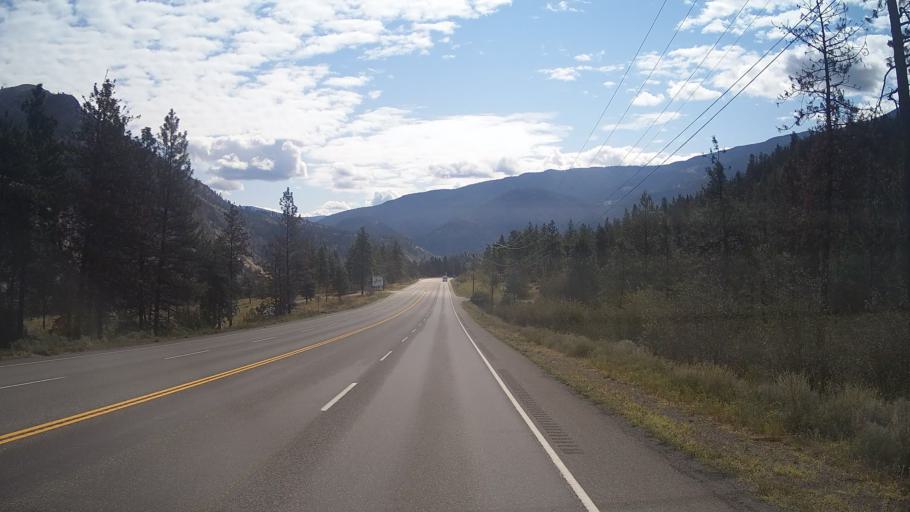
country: CA
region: British Columbia
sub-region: Thompson-Nicola Regional District
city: Ashcroft
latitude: 50.2596
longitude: -121.5363
